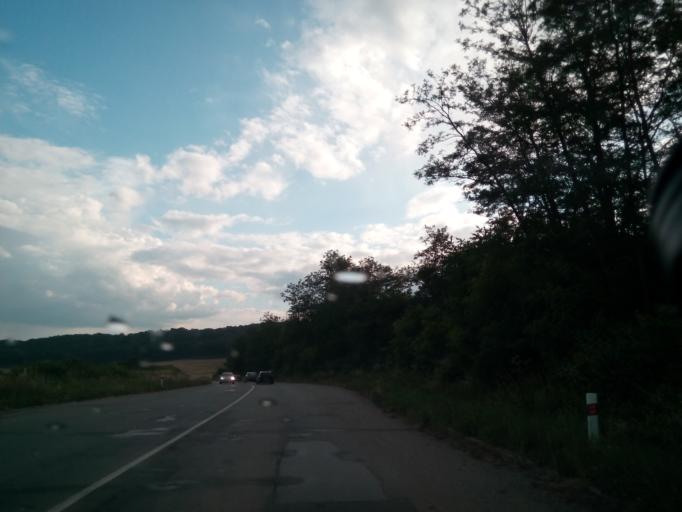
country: SK
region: Kosicky
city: Kosice
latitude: 48.6575
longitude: 21.3803
